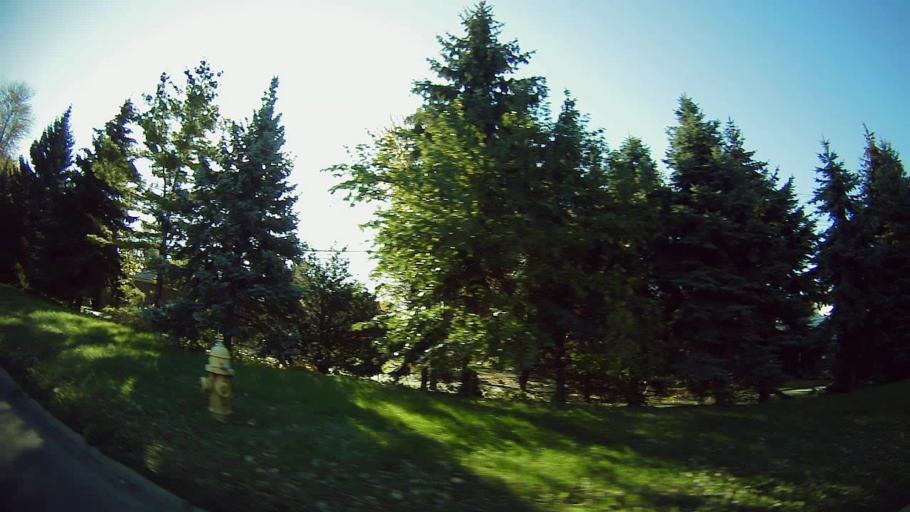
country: US
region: Michigan
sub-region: Wayne County
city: Dearborn Heights
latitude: 42.3269
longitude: -83.2579
